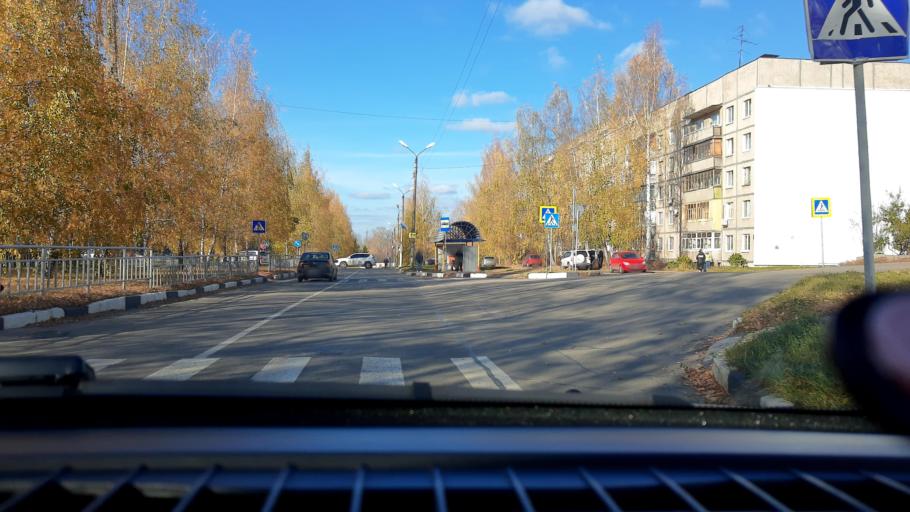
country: RU
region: Nizjnij Novgorod
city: Kstovo
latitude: 56.1569
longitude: 44.2119
